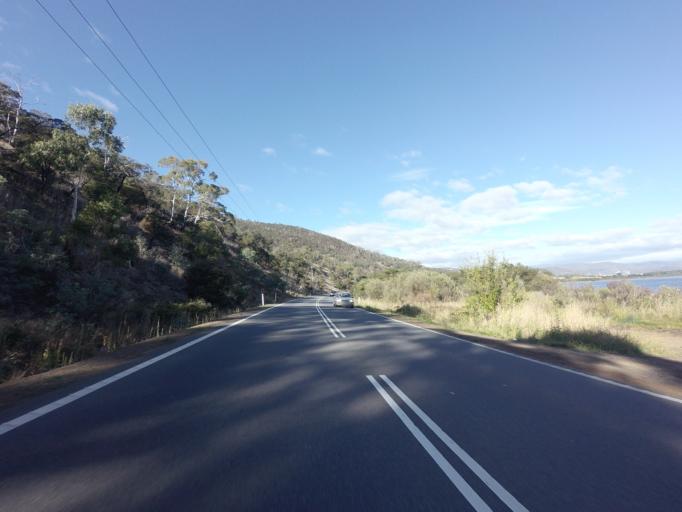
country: AU
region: Tasmania
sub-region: Derwent Valley
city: New Norfolk
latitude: -42.7679
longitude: 147.1433
